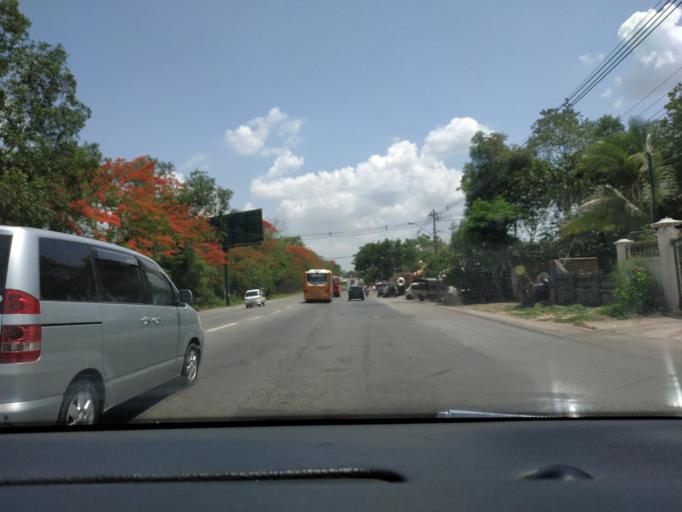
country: MM
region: Yangon
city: Yangon
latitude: 16.9964
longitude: 96.1305
